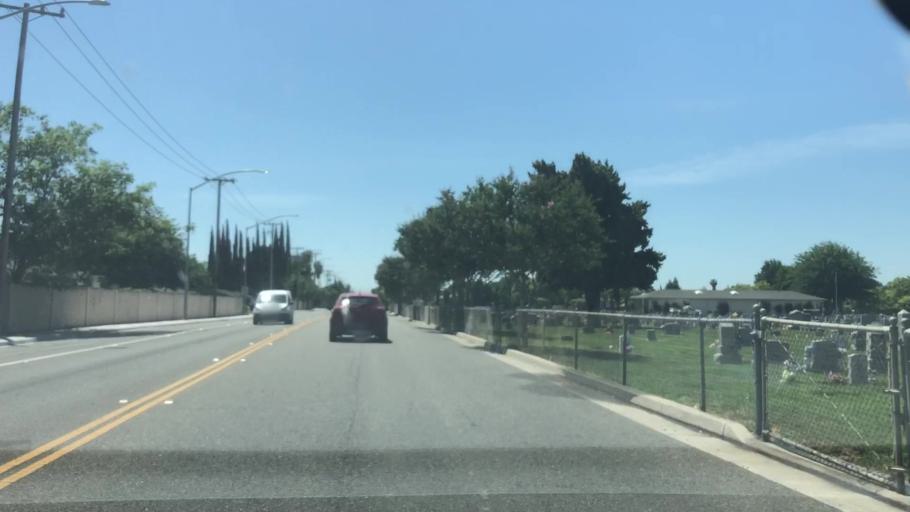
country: US
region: California
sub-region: San Joaquin County
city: Tracy
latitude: 37.7252
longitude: -121.4170
